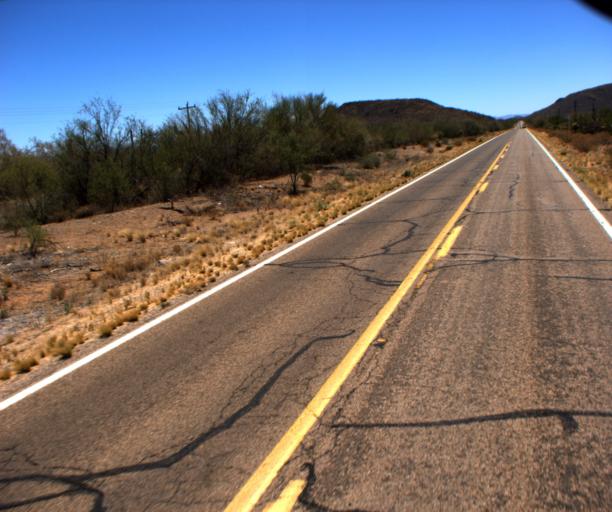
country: US
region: Arizona
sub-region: Pima County
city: Sells
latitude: 31.9778
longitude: -111.9666
